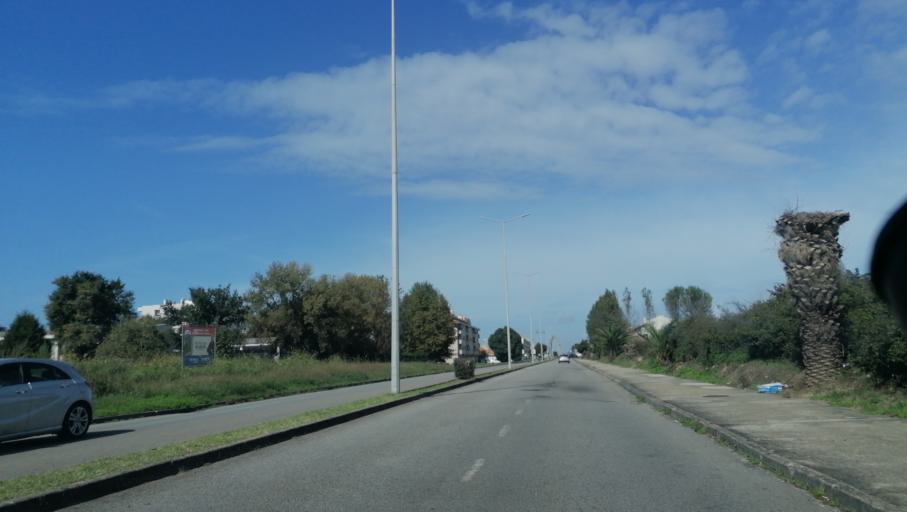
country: PT
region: Aveiro
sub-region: Espinho
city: Espinho
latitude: 41.0015
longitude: -8.6343
